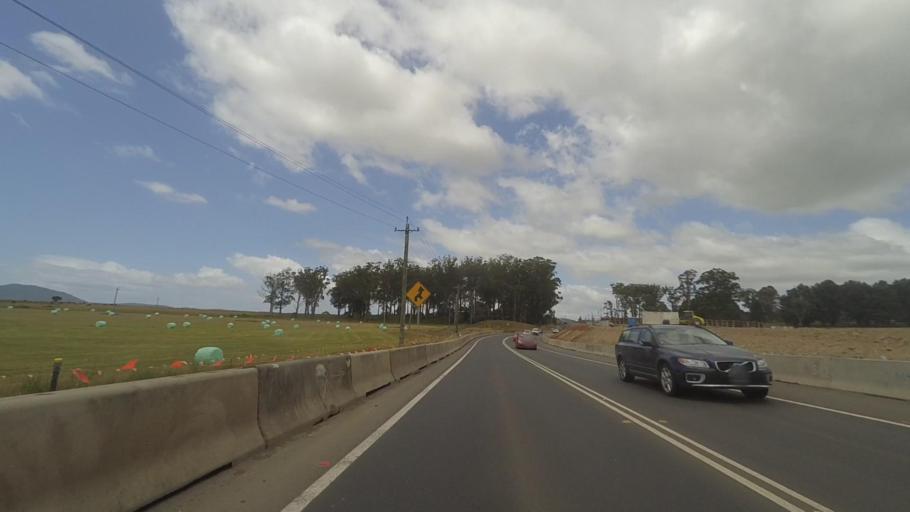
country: AU
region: New South Wales
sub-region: Shoalhaven Shire
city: Berry
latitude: -34.7804
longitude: 150.6807
